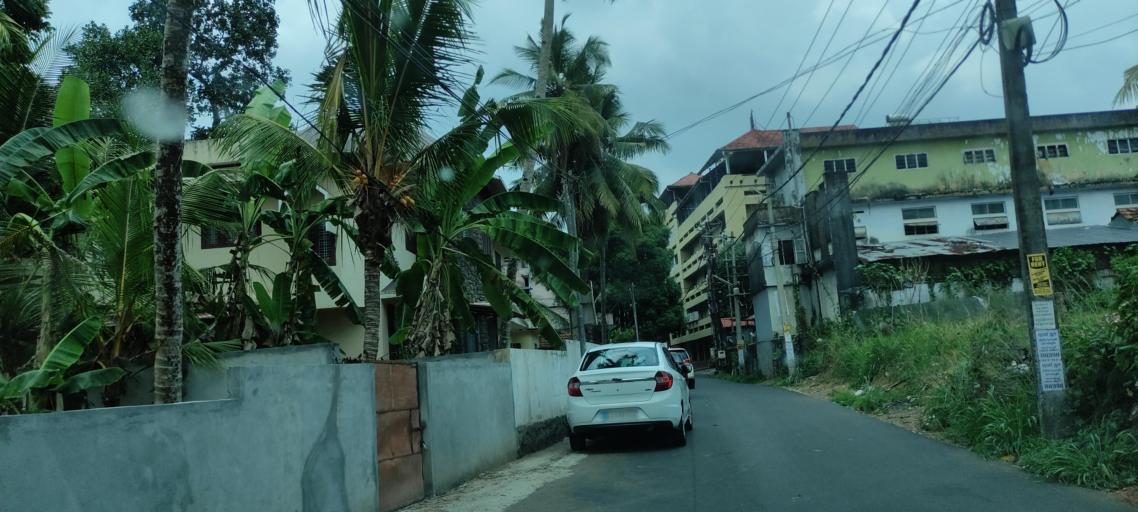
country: IN
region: Kerala
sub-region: Pattanamtitta
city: Adur
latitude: 9.1559
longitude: 76.7296
